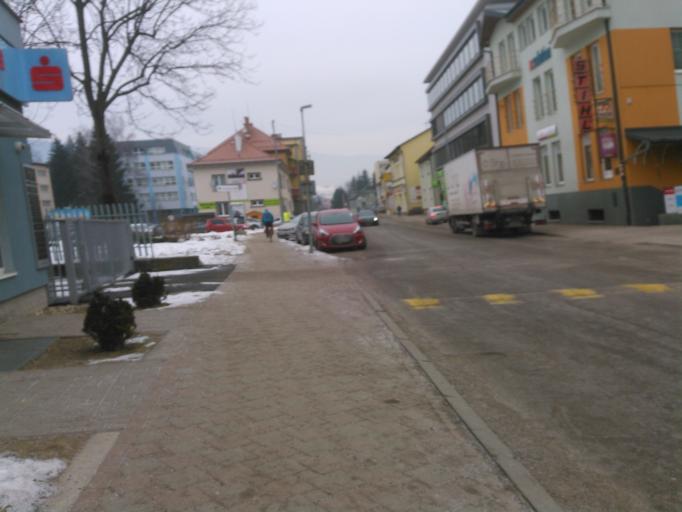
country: SK
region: Zilinsky
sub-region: Okres Dolny Kubin
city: Dolny Kubin
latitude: 49.2107
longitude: 19.2937
